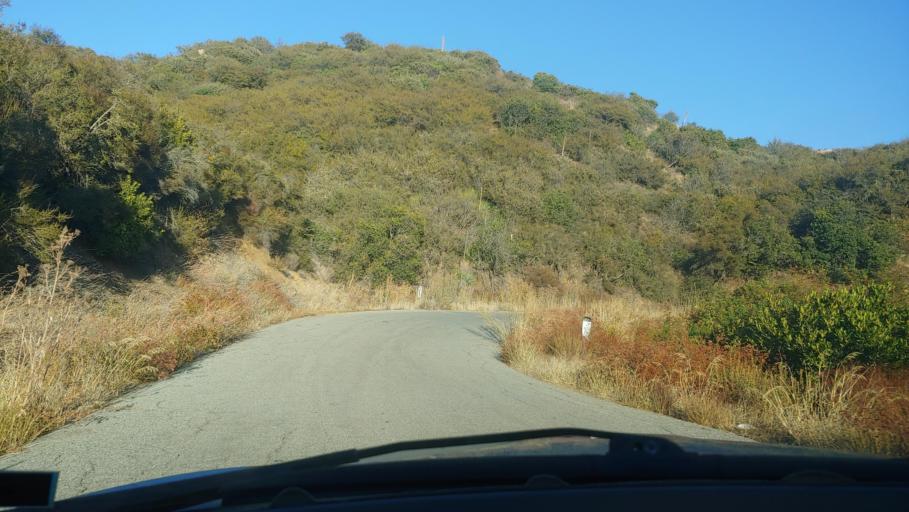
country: US
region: California
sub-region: Santa Barbara County
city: Goleta
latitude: 34.5156
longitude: -119.7952
